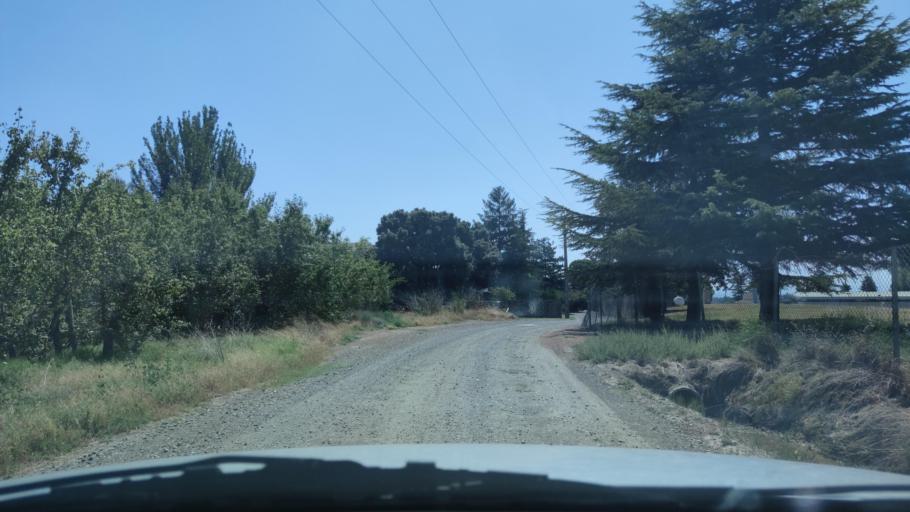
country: ES
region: Catalonia
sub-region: Provincia de Lleida
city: Alpicat
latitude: 41.6486
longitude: 0.5714
